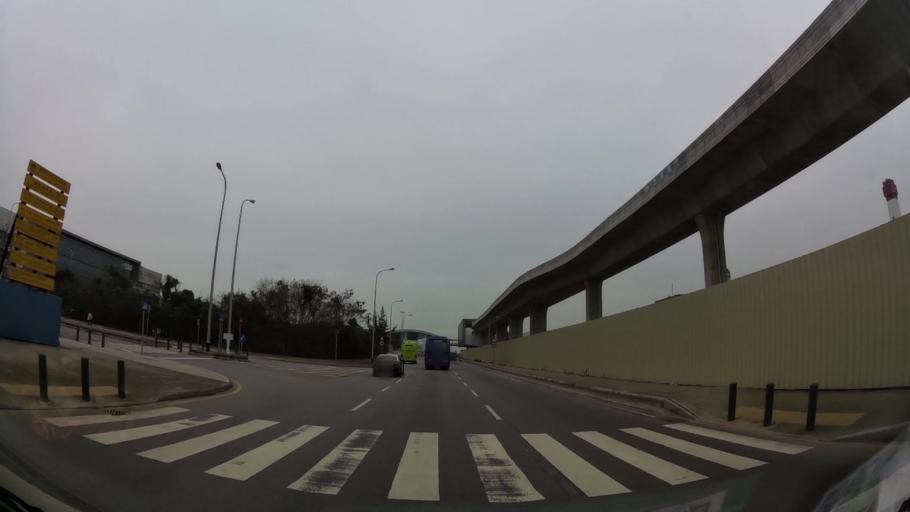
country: MO
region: Macau
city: Macau
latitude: 22.1639
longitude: 113.5713
